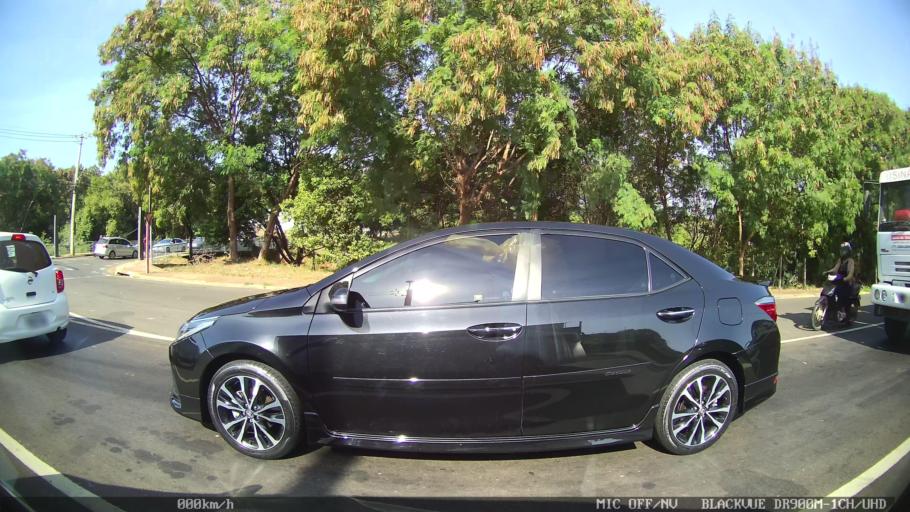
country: BR
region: Sao Paulo
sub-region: Sao Jose Do Rio Preto
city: Sao Jose do Rio Preto
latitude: -20.7926
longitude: -49.3938
